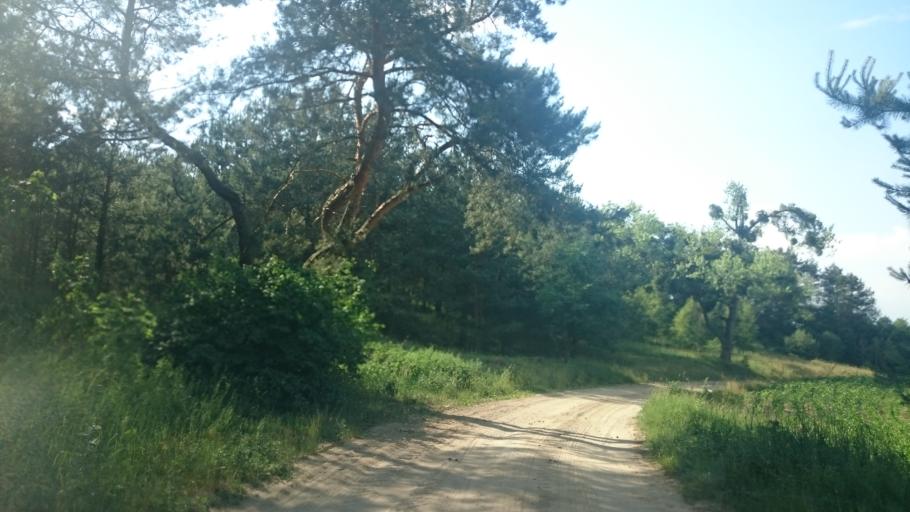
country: PL
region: Kujawsko-Pomorskie
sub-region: Powiat golubsko-dobrzynski
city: Radomin
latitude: 53.1249
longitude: 19.1378
